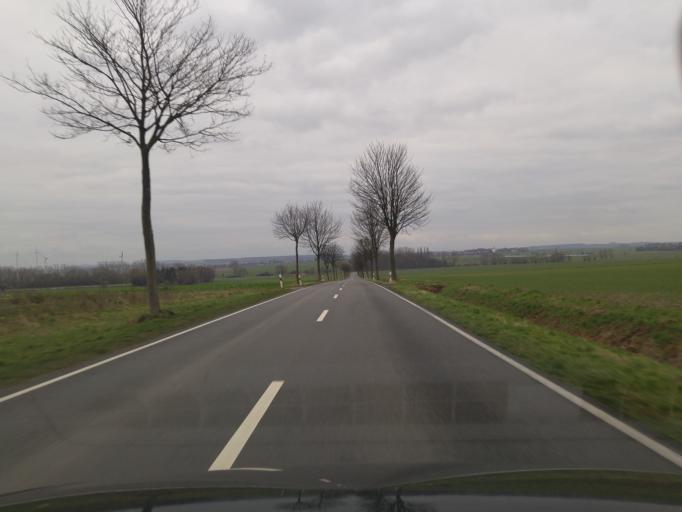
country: DE
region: Lower Saxony
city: Ilsede
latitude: 52.2409
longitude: 10.1689
